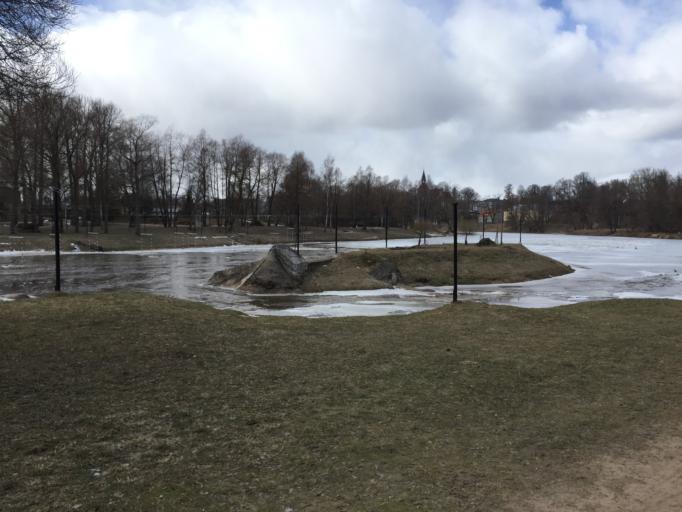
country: LV
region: Valmieras Rajons
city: Valmiera
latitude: 57.5363
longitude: 25.4352
